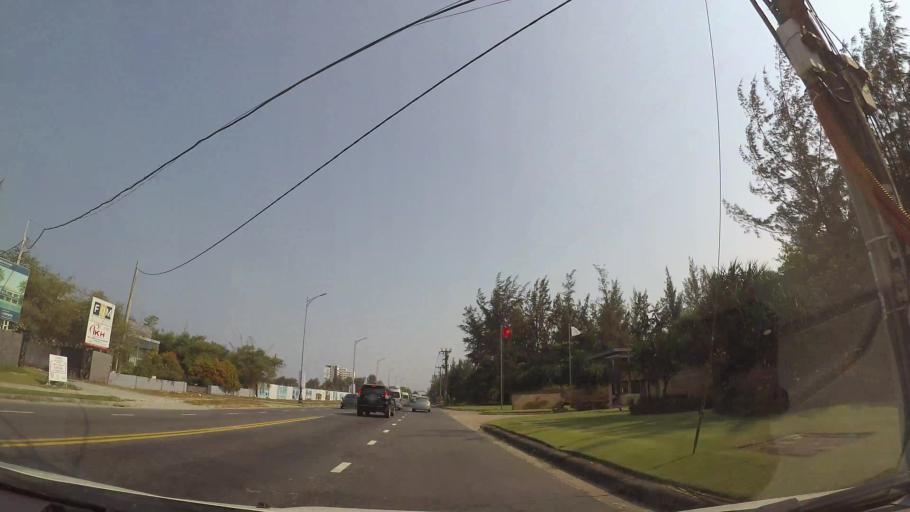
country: VN
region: Da Nang
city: Ngu Hanh Son
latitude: 15.9730
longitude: 108.2806
